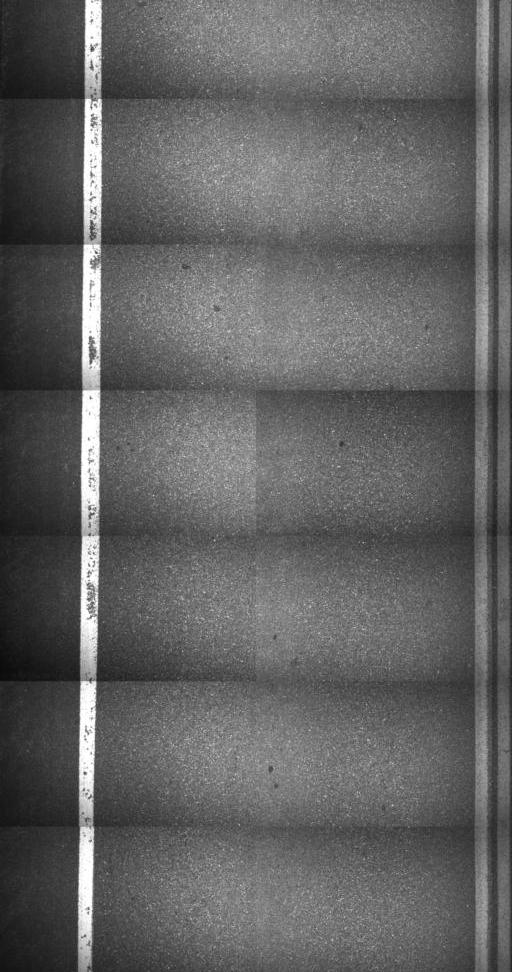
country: US
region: Vermont
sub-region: Caledonia County
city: Lyndonville
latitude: 44.8147
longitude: -71.8646
